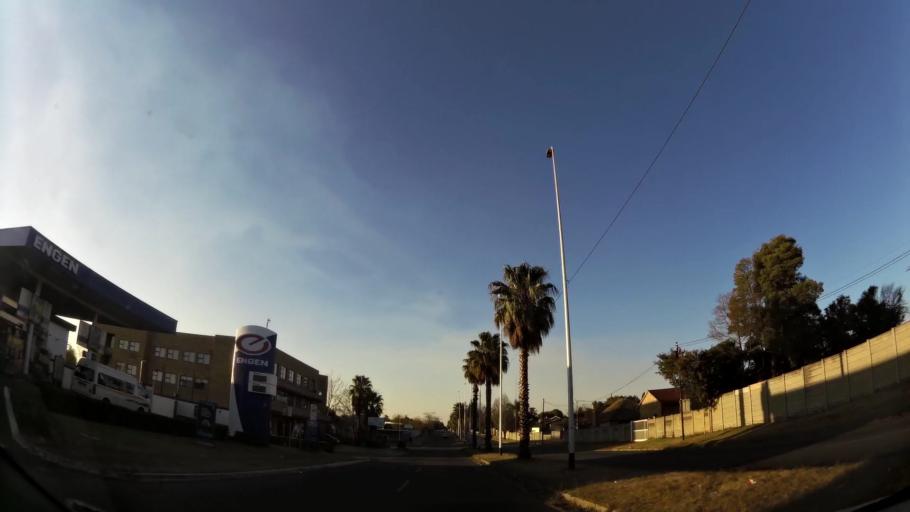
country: ZA
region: Gauteng
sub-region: City of Johannesburg Metropolitan Municipality
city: Roodepoort
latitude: -26.1497
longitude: 27.8786
